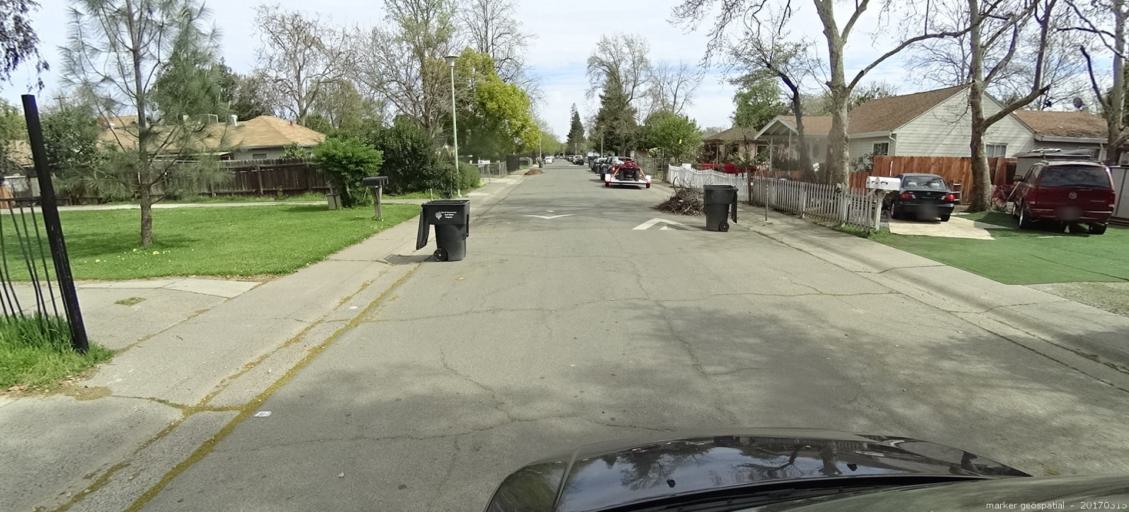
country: US
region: California
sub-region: Sacramento County
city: Parkway
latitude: 38.5224
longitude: -121.4761
